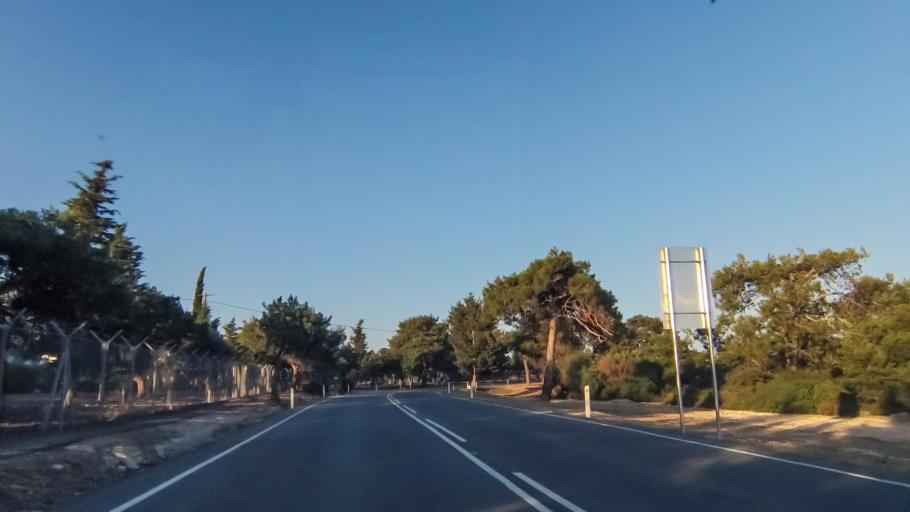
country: CY
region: Limassol
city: Sotira
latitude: 34.6734
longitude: 32.8323
